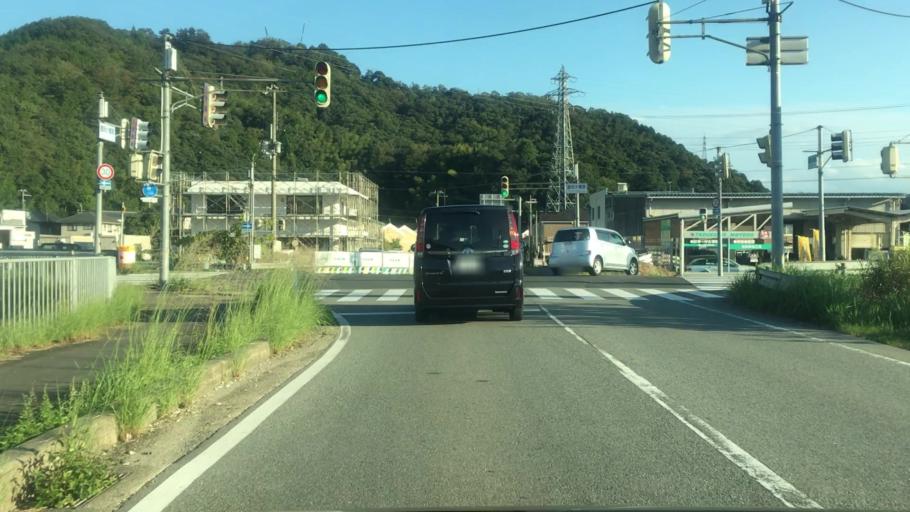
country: JP
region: Hyogo
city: Toyooka
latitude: 35.5591
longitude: 134.8245
